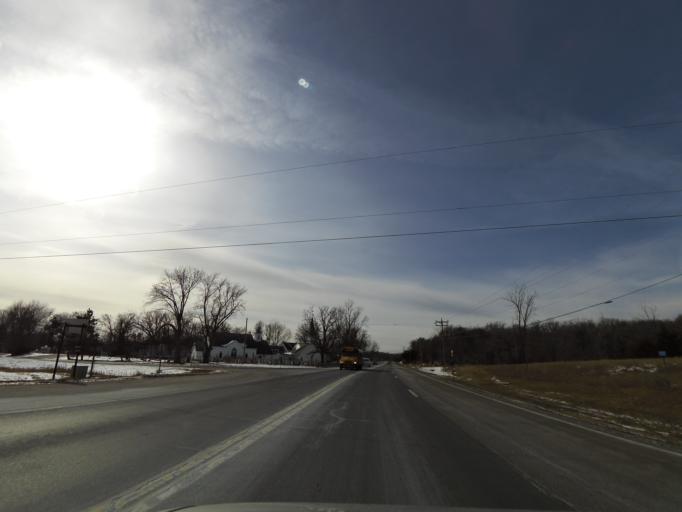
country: US
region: Minnesota
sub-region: Washington County
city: Lake Elmo
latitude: 44.9682
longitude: -92.8571
